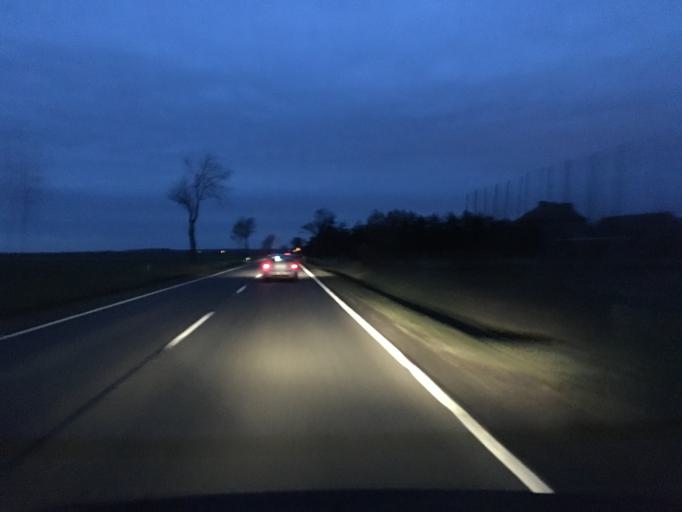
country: PL
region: Opole Voivodeship
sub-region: Powiat brzeski
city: Losiow
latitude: 50.8032
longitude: 17.5416
